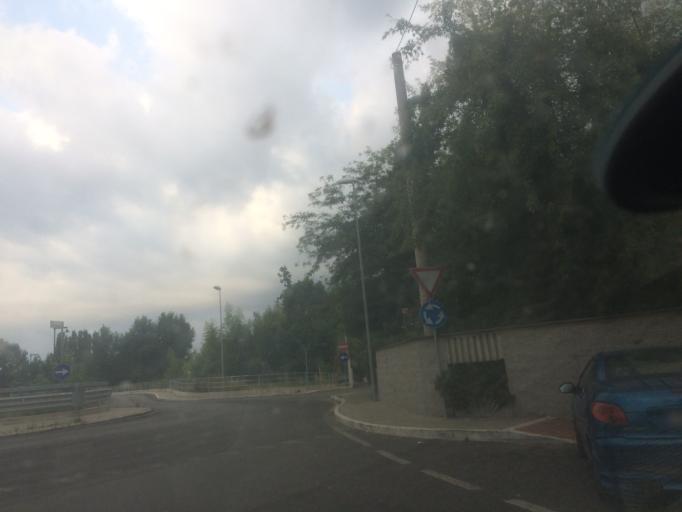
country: IT
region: Tuscany
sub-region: Provincia di Massa-Carrara
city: Massa
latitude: 44.0199
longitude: 10.0970
